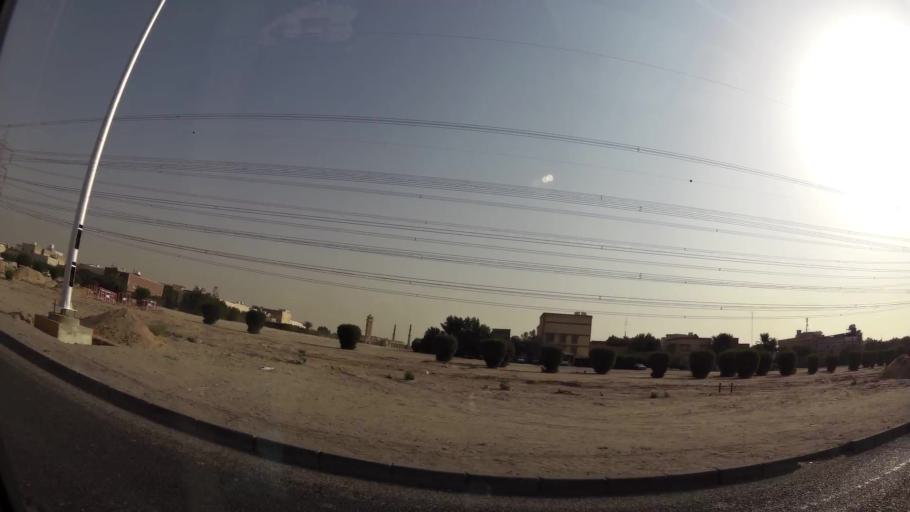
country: KW
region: Al Asimah
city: Ar Rabiyah
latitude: 29.2959
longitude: 47.8708
